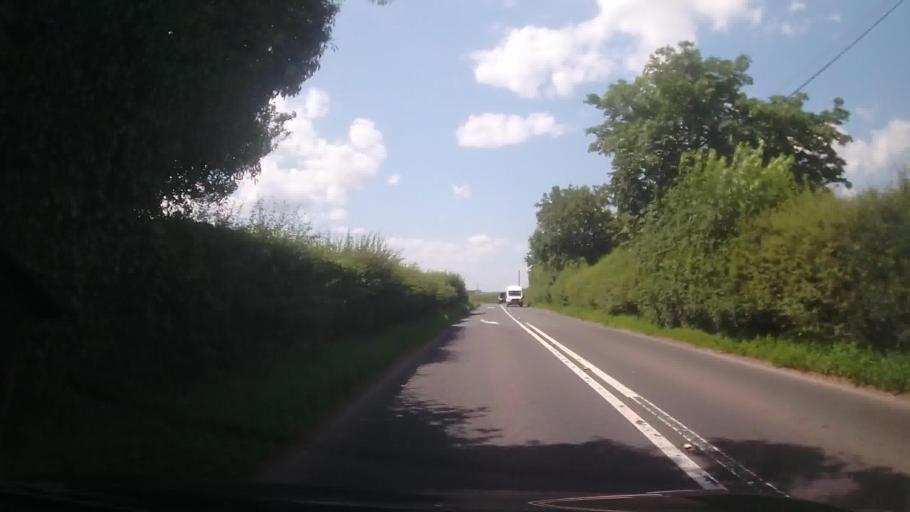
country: GB
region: England
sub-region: Herefordshire
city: Bodenham
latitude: 52.1571
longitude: -2.6584
